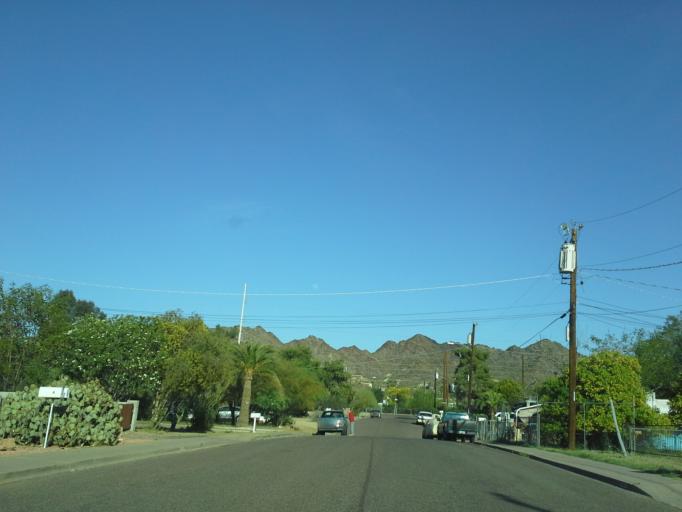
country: US
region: Arizona
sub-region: Maricopa County
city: Paradise Valley
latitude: 33.5775
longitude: -112.0586
